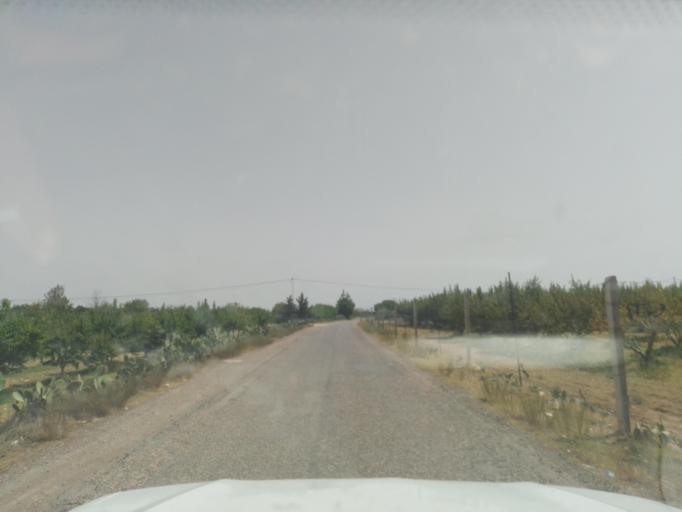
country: TN
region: Al Qasrayn
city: Kasserine
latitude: 35.2684
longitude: 9.0017
